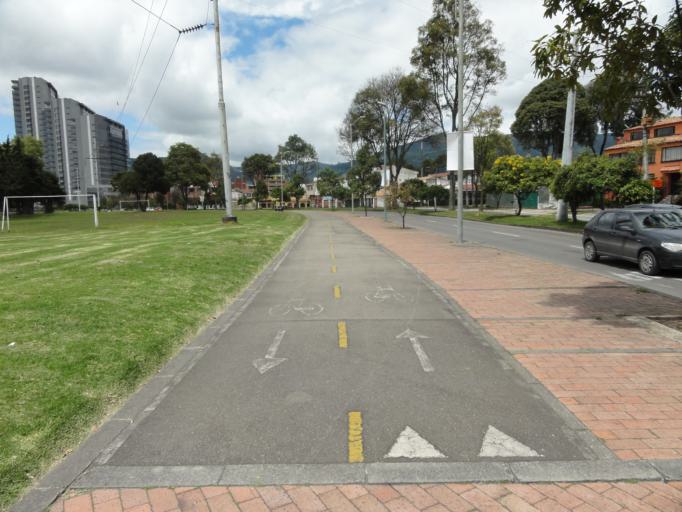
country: CO
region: Bogota D.C.
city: Barrio San Luis
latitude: 4.6962
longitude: -74.0604
